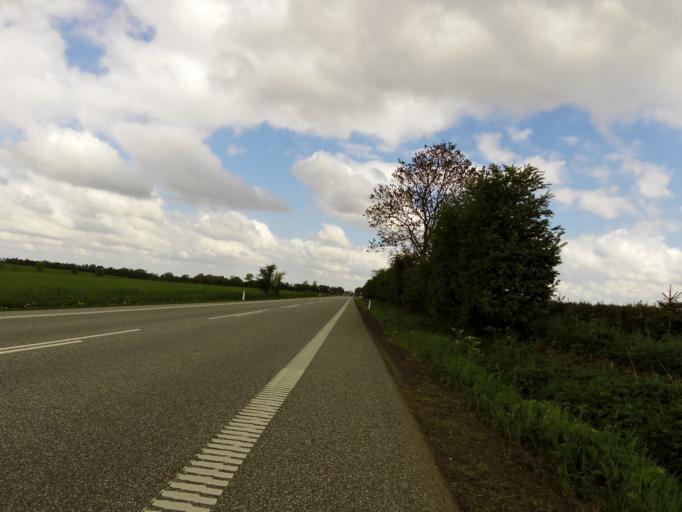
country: DK
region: South Denmark
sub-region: Haderslev Kommune
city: Gram
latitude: 55.2783
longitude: 9.0282
